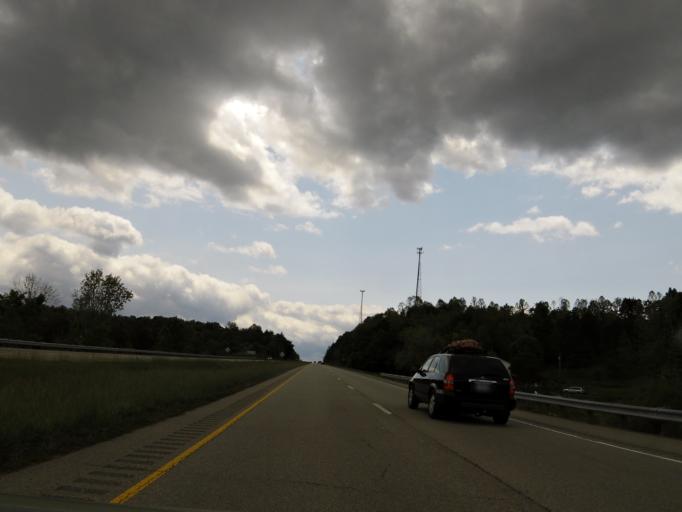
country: US
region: Ohio
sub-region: Meigs County
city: Pomeroy
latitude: 39.1360
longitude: -82.0213
